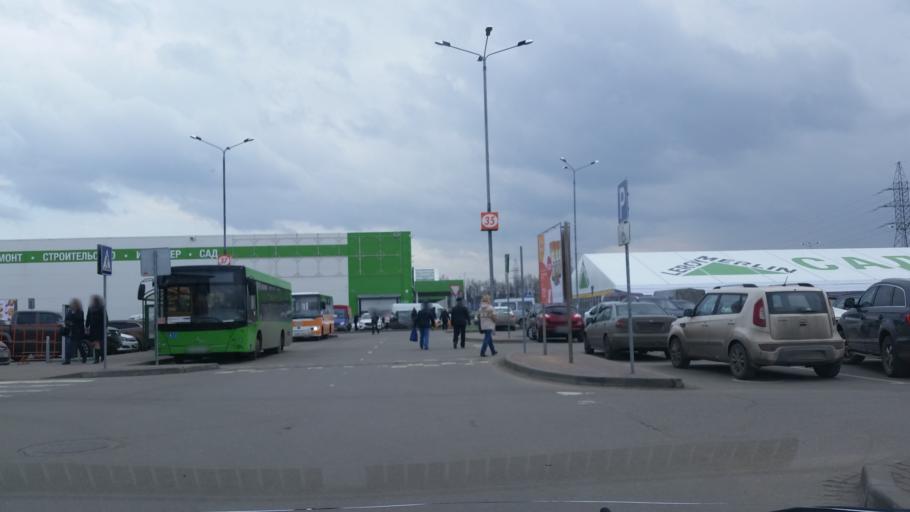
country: RU
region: Moskovskaya
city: Arkhangel'skoye
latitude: 55.8011
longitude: 37.2991
